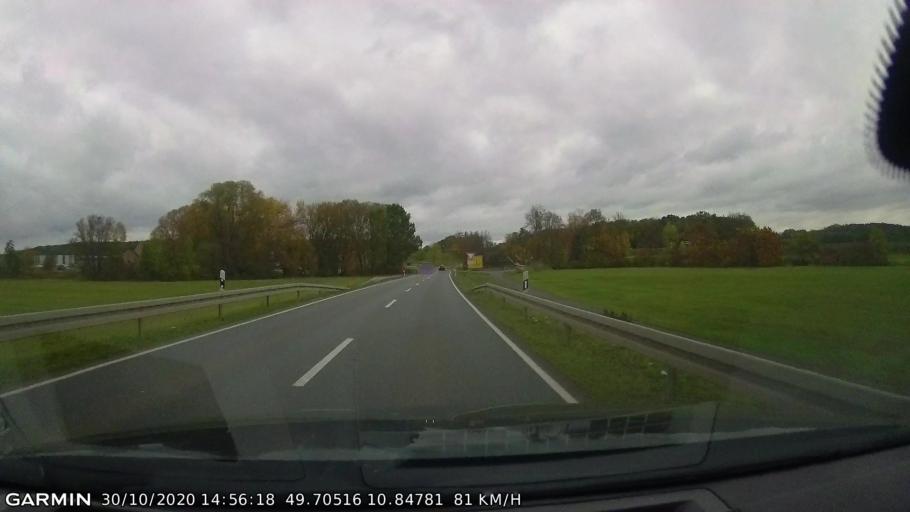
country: DE
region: Bavaria
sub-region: Regierungsbezirk Mittelfranken
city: Gremsdorf
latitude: 49.7051
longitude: 10.8483
